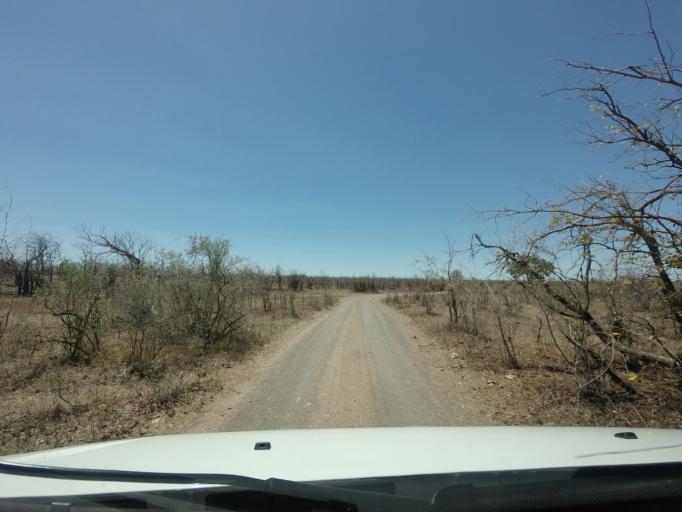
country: ZA
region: Limpopo
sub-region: Mopani District Municipality
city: Phalaborwa
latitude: -23.5845
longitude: 31.4470
